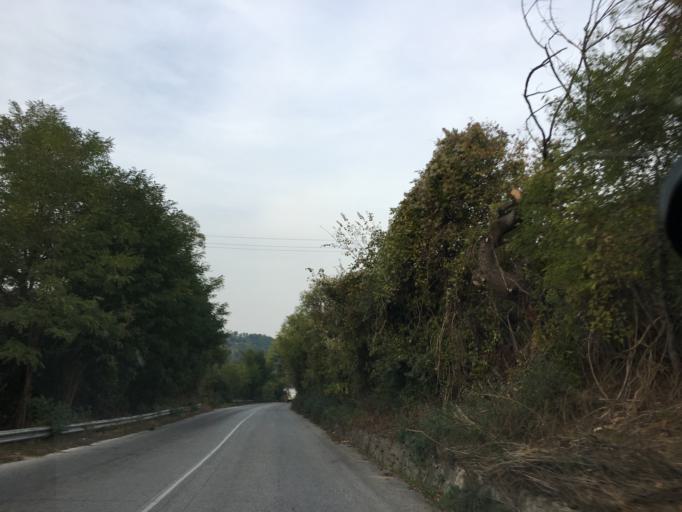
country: BG
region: Pazardzhik
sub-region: Obshtina Belovo
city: Belovo
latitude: 42.2049
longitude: 23.9979
